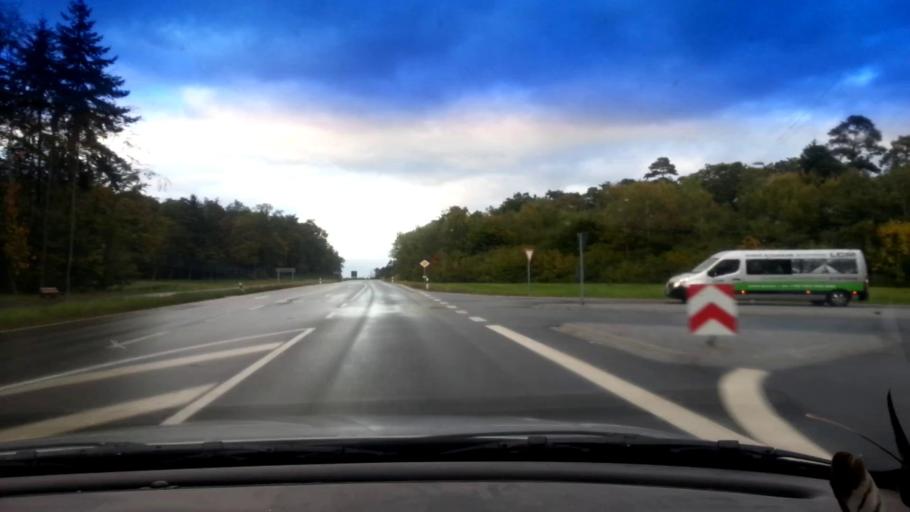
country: DE
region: Bavaria
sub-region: Upper Franconia
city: Burgebrach
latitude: 49.8079
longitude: 10.7319
